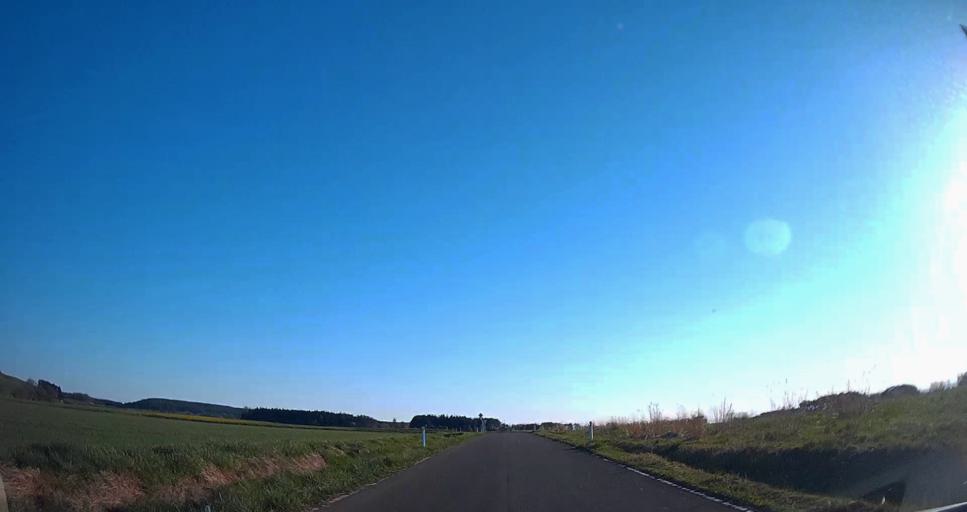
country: JP
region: Aomori
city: Mutsu
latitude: 41.1171
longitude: 141.2752
